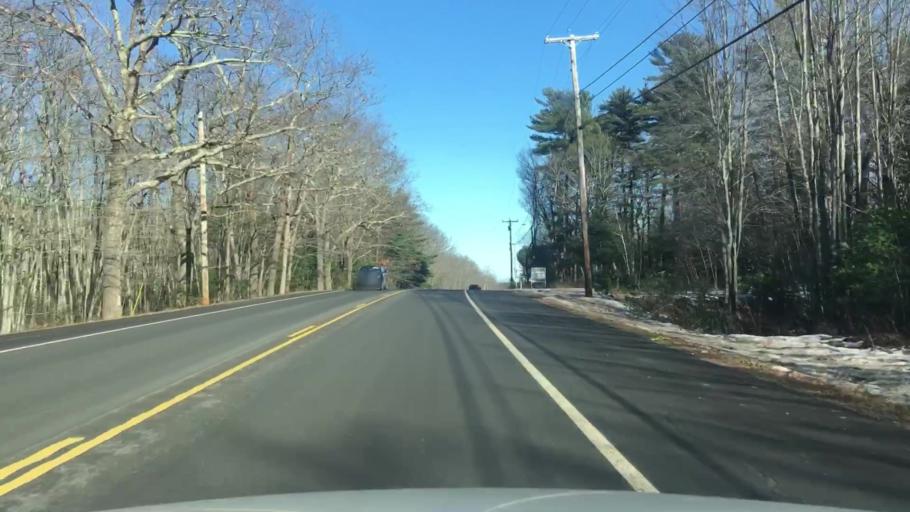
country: US
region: Maine
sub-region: York County
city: Arundel
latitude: 43.4447
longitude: -70.5011
